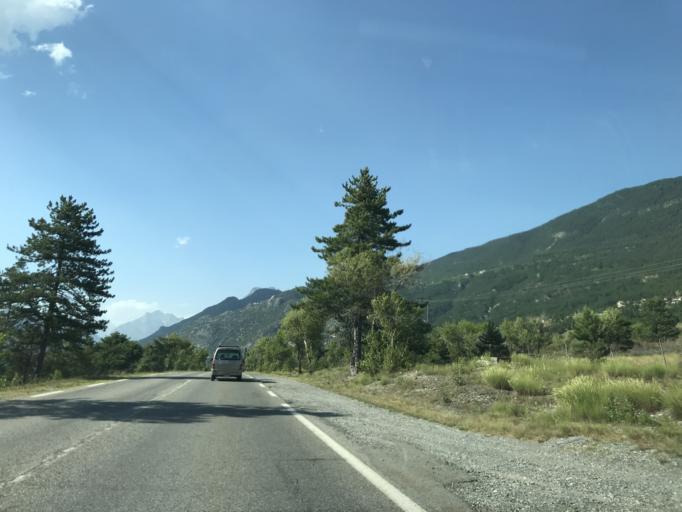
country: FR
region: Provence-Alpes-Cote d'Azur
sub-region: Departement des Hautes-Alpes
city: Guillestre
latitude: 44.6895
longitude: 6.6129
